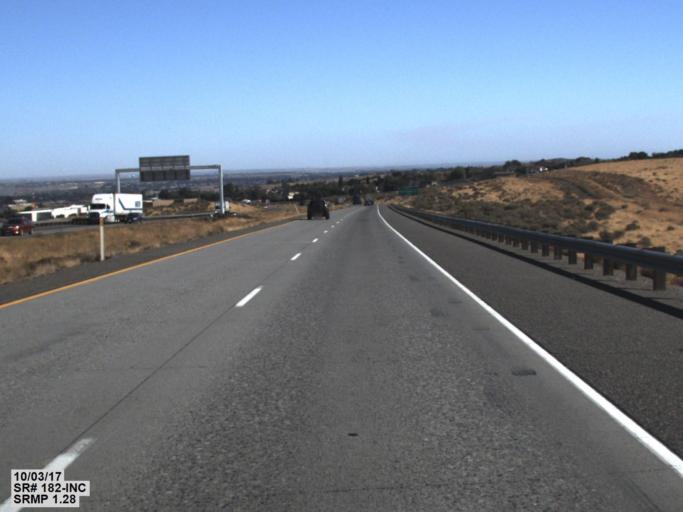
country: US
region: Washington
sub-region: Benton County
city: West Richland
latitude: 46.2464
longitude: -119.3362
